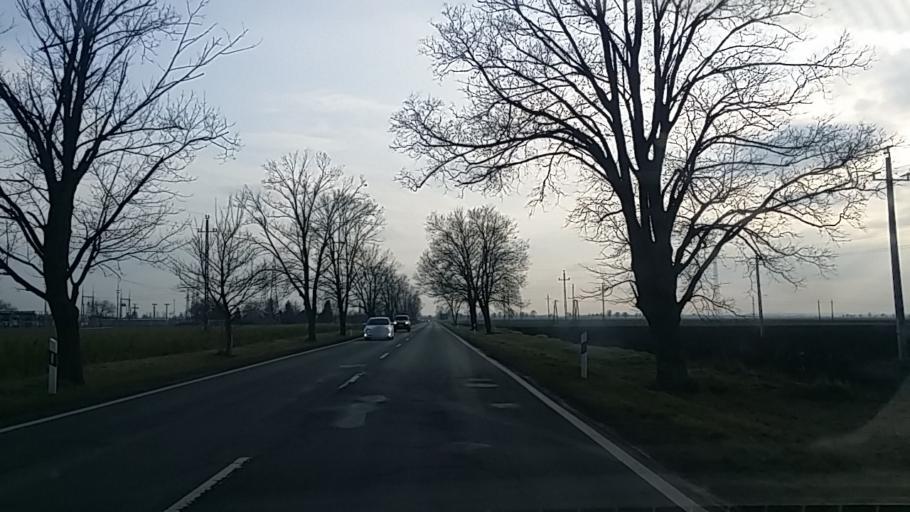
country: HU
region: Baranya
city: Lanycsok
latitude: 46.0113
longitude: 18.6555
